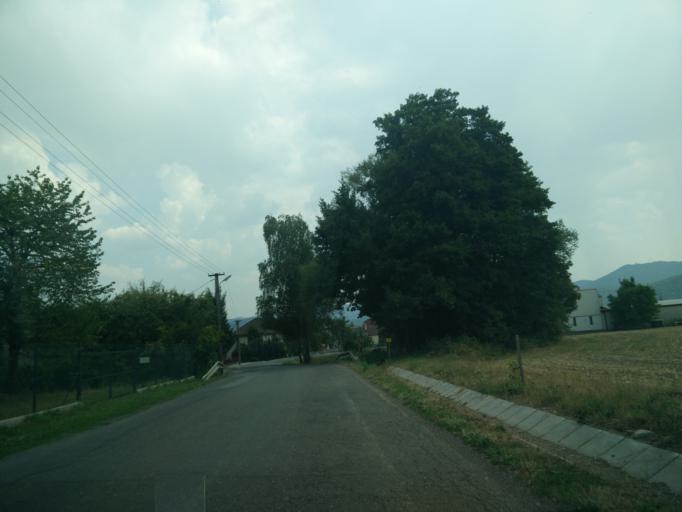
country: SK
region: Banskobystricky
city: Zarnovica
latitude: 48.5517
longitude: 18.7583
